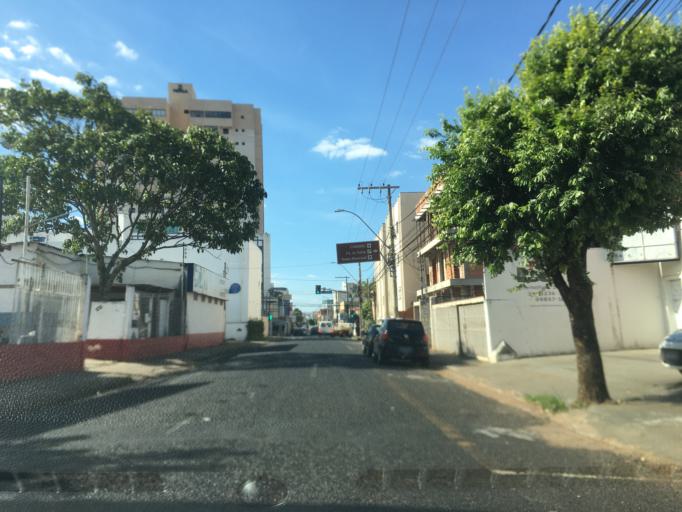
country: BR
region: Minas Gerais
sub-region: Uberlandia
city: Uberlandia
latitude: -18.9180
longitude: -48.2697
